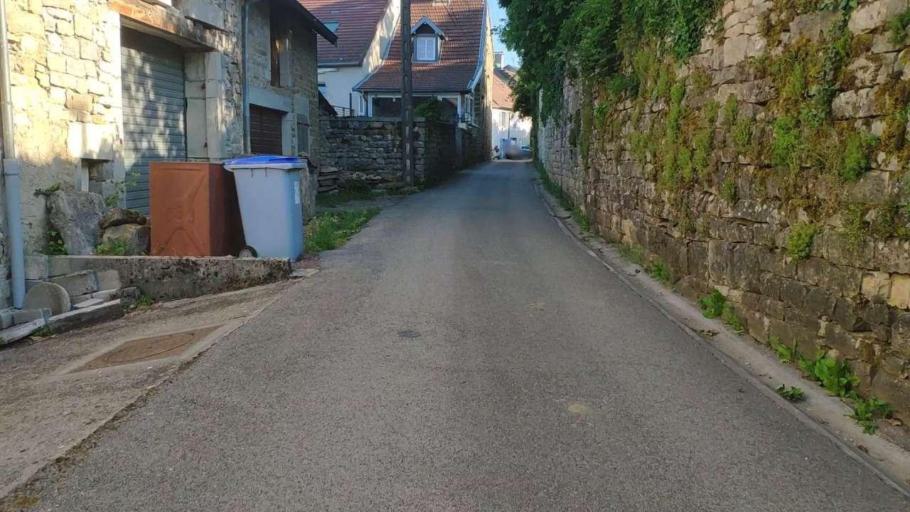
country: FR
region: Franche-Comte
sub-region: Departement du Jura
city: Perrigny
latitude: 46.7150
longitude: 5.5953
